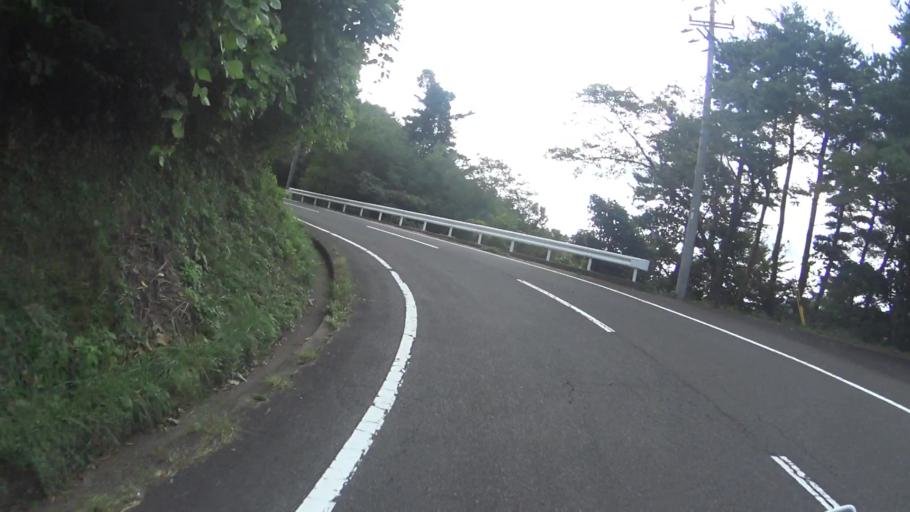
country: JP
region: Kyoto
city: Miyazu
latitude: 35.7342
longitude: 135.1758
